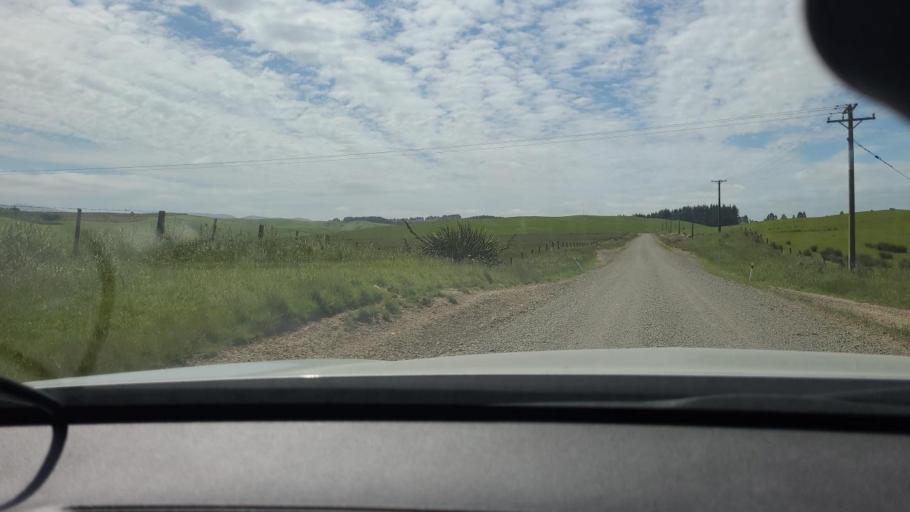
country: NZ
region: Southland
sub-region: Southland District
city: Riverton
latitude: -45.9438
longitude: 167.8919
